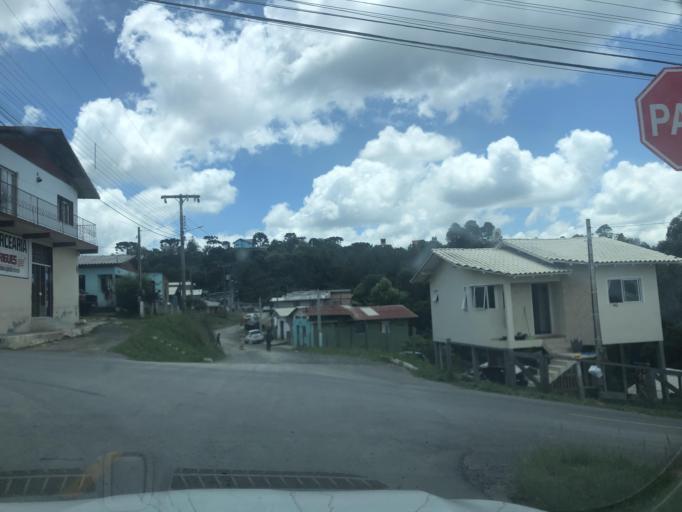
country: BR
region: Santa Catarina
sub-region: Lages
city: Lages
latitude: -27.7857
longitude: -50.3151
